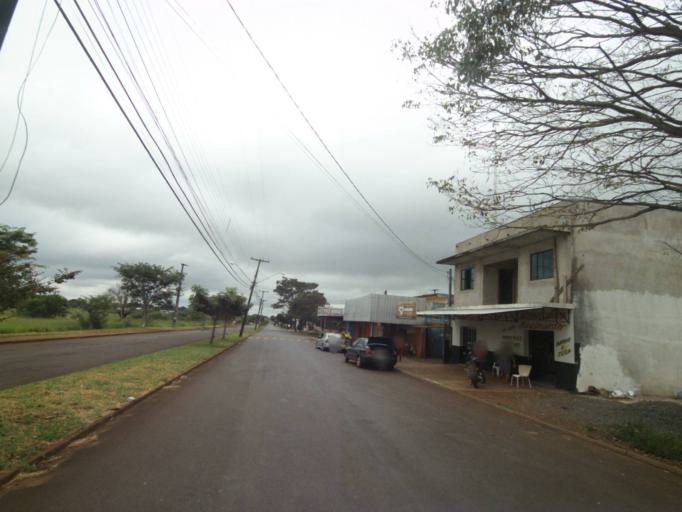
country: BR
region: Parana
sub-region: Campo Mourao
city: Campo Mourao
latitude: -24.0151
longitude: -52.3556
